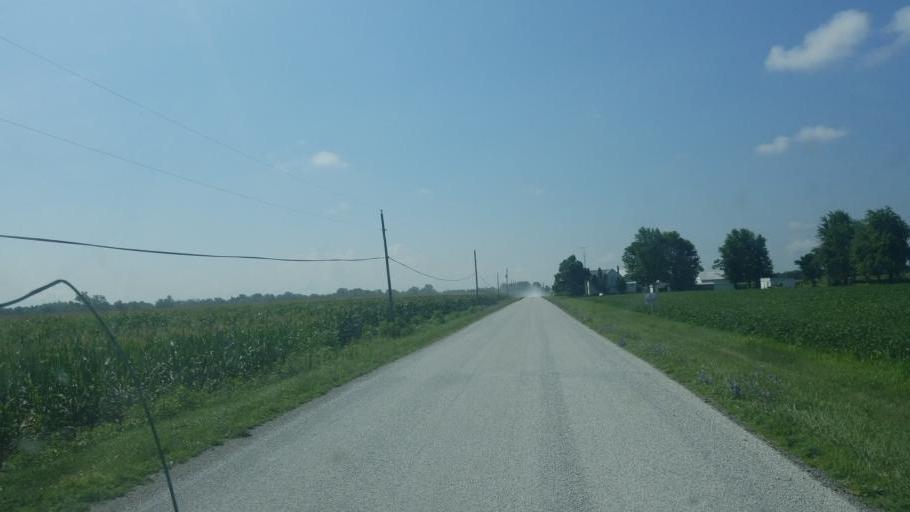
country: US
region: Ohio
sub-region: Hardin County
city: Ada
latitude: 40.6929
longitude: -83.7305
